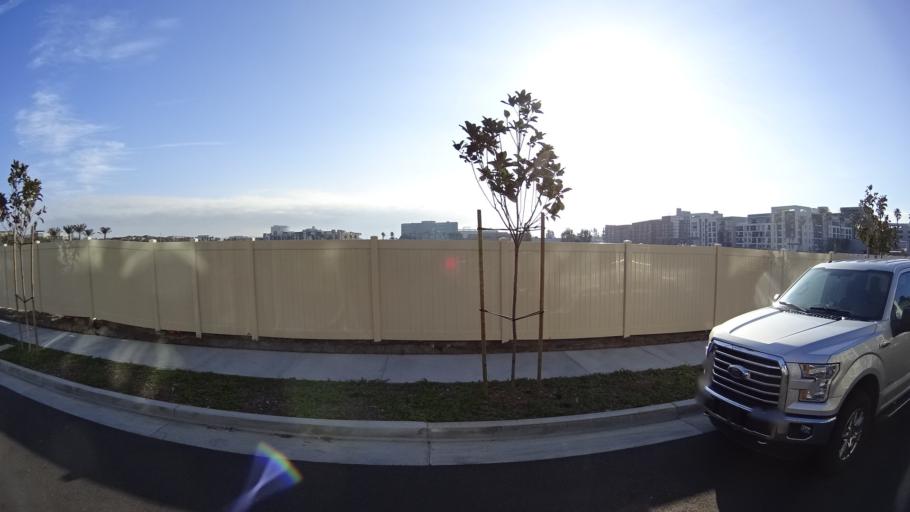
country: US
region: California
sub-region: Orange County
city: Anaheim
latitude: 33.8012
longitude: -117.8950
